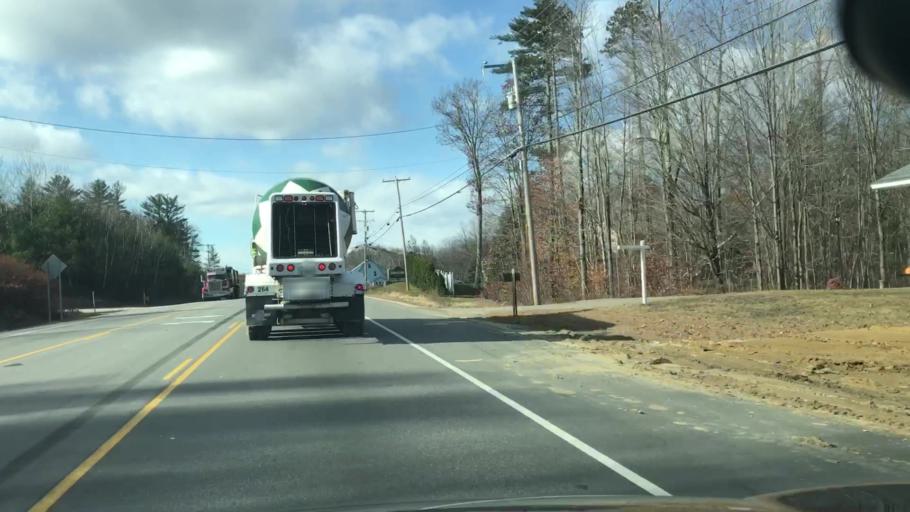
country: US
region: New Hampshire
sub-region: Merrimack County
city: Chichester
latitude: 43.2477
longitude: -71.4138
